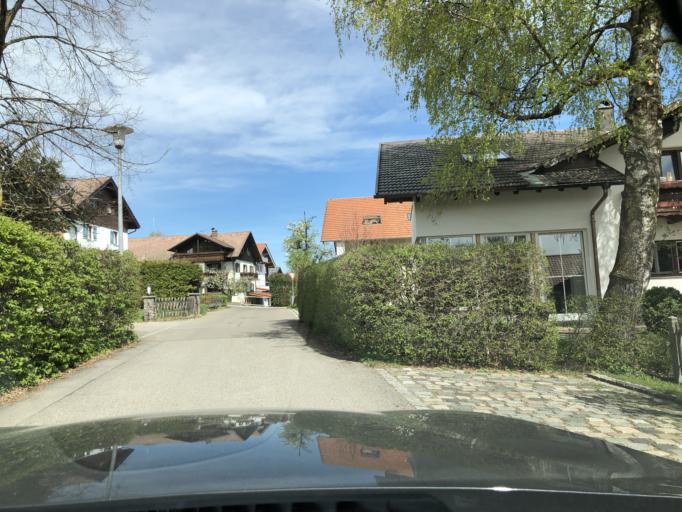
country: DE
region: Bavaria
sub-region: Swabia
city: Seeg
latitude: 47.6543
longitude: 10.6121
